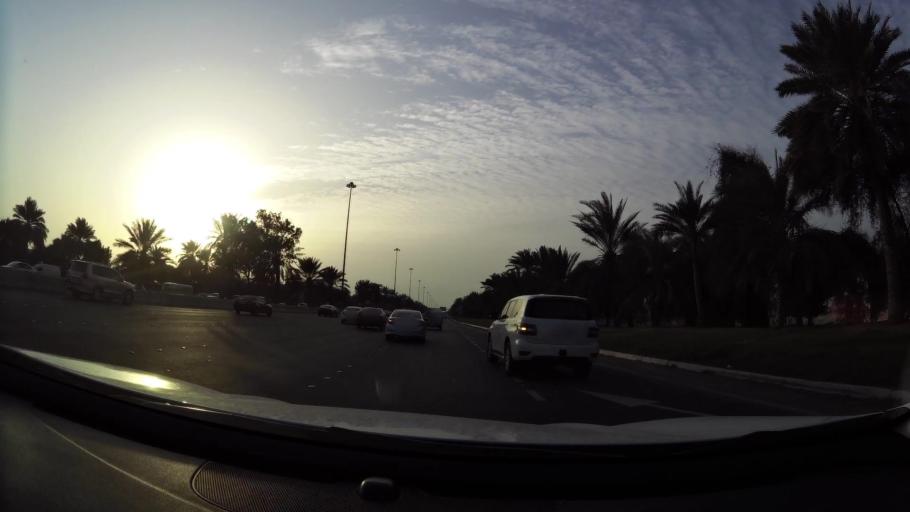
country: AE
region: Abu Dhabi
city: Abu Dhabi
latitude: 24.3953
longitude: 54.5164
